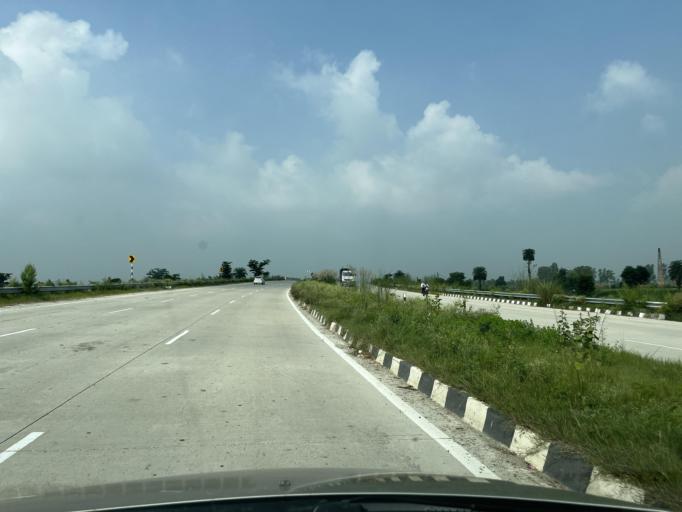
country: IN
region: Uttarakhand
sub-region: Udham Singh Nagar
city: Kashipur
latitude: 29.1635
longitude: 78.9669
